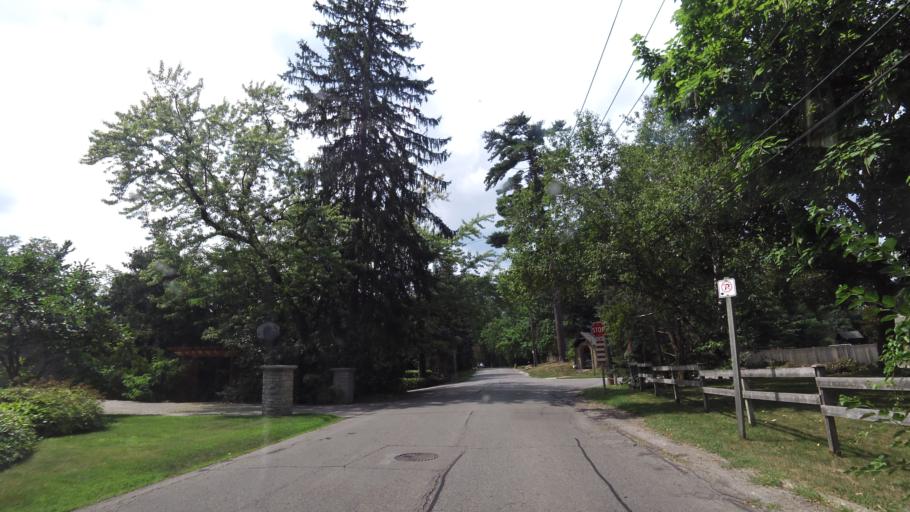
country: CA
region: Ontario
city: Mississauga
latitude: 43.5546
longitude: -79.5978
